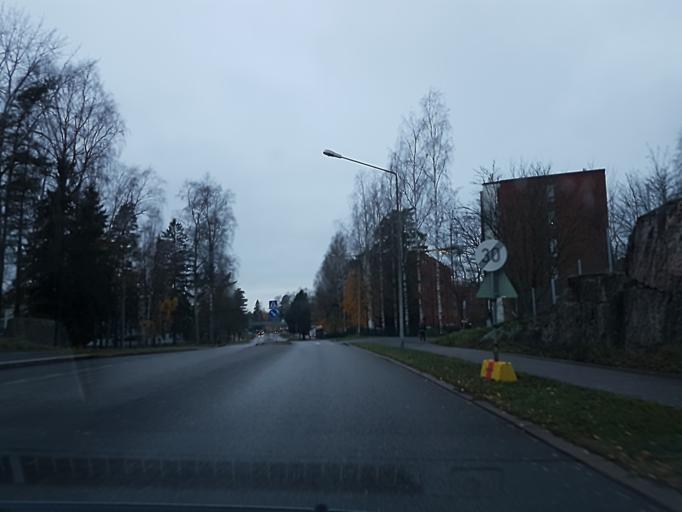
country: FI
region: Uusimaa
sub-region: Helsinki
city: Vantaa
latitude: 60.2370
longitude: 25.1215
